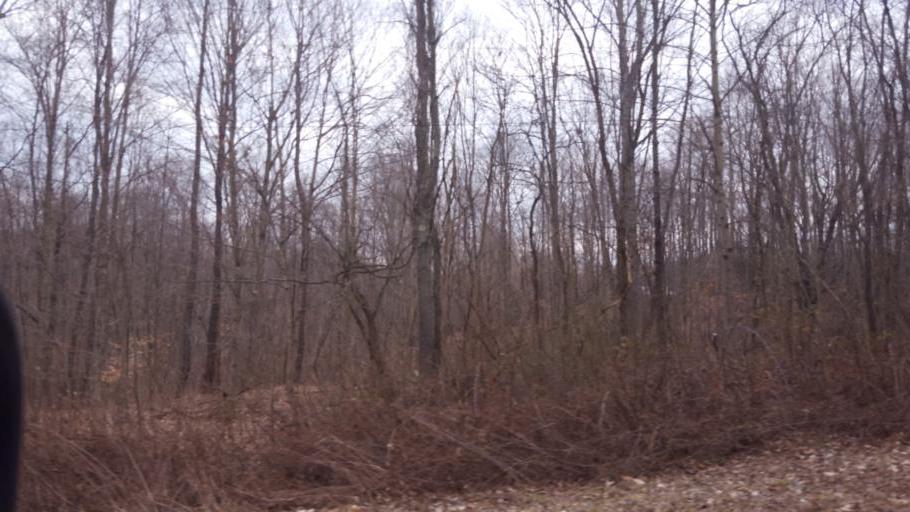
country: US
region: Ohio
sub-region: Ashland County
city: Loudonville
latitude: 40.7193
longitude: -82.3463
